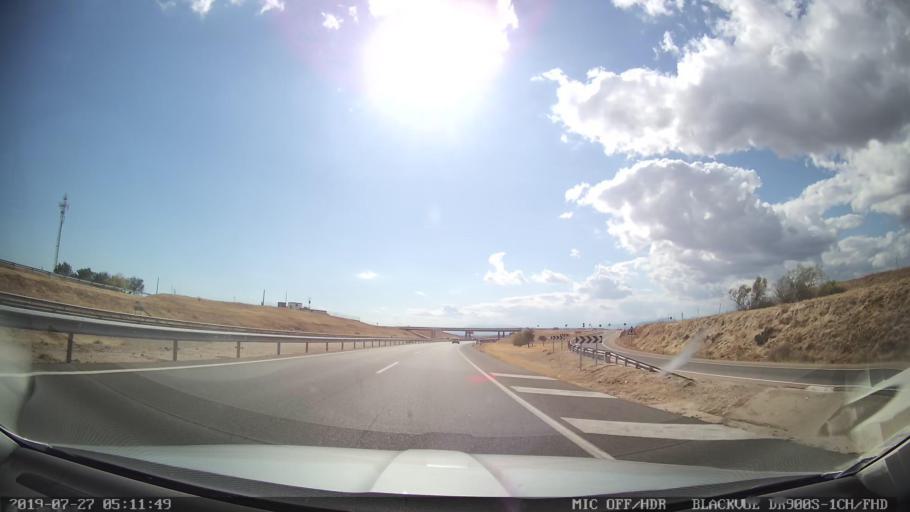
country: ES
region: Castille-La Mancha
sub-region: Province of Toledo
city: Quismondo
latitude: 40.1132
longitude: -4.3103
